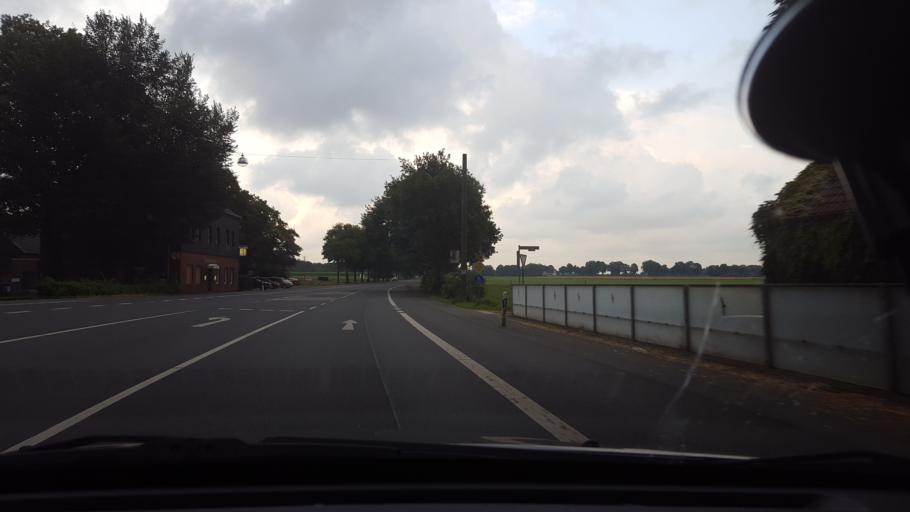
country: DE
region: North Rhine-Westphalia
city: Herten
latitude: 51.6332
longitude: 7.1426
